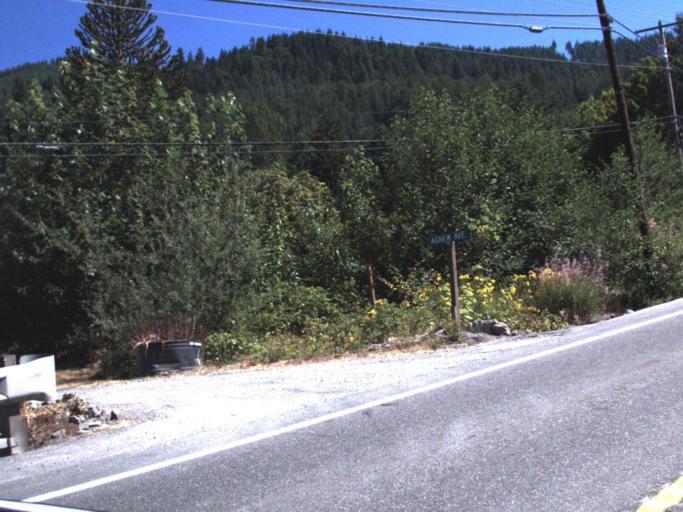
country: US
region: Washington
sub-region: King County
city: Fall City
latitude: 47.5685
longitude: -121.8804
